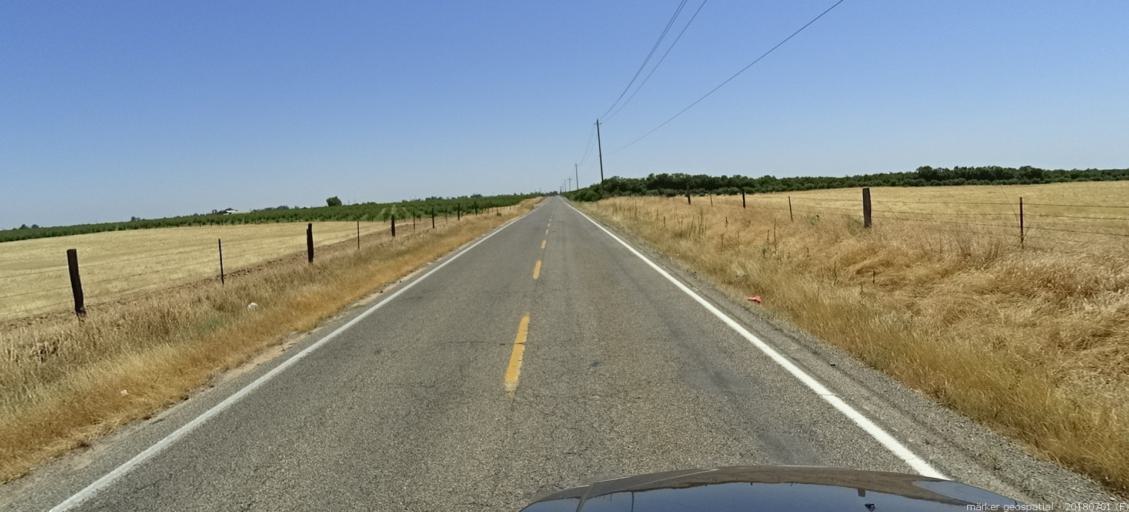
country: US
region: California
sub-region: Madera County
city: Madera Acres
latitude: 37.0119
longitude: -120.0288
